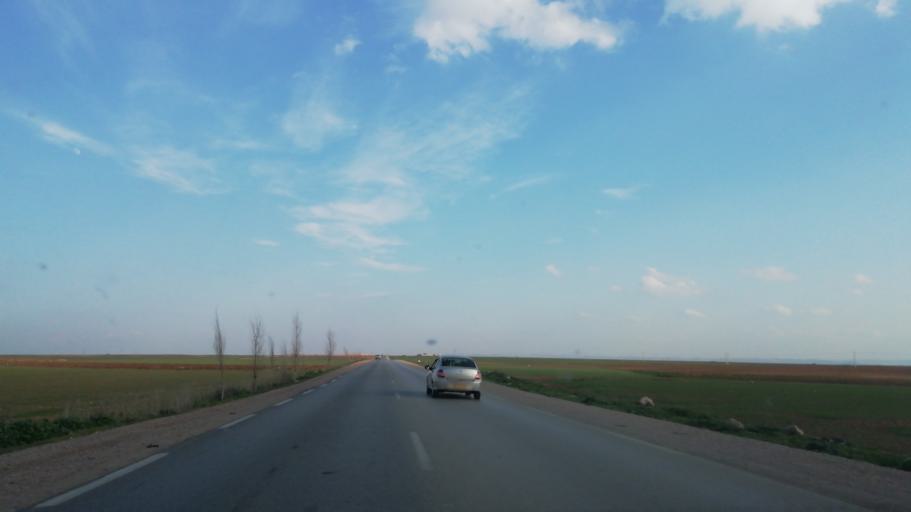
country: DZ
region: Relizane
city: Relizane
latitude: 35.8966
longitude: 0.5953
